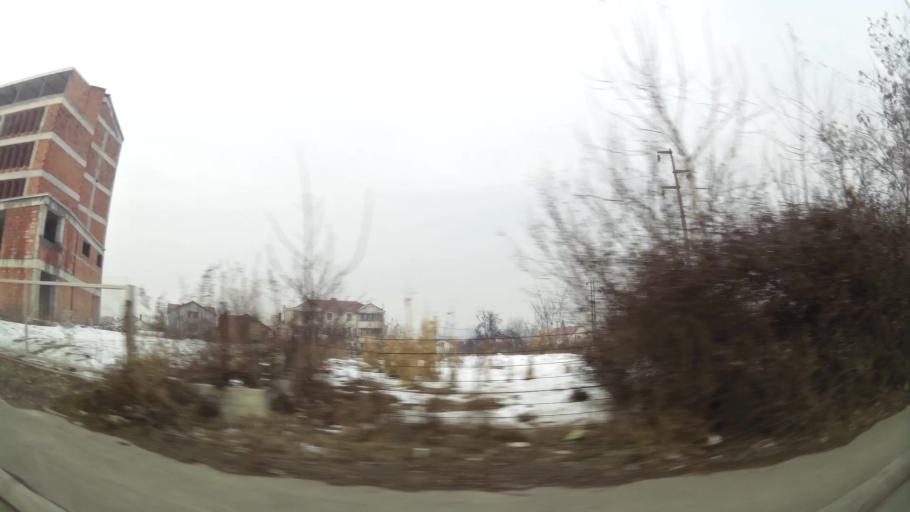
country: MK
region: Suto Orizari
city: Suto Orizare
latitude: 42.0271
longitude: 21.4230
